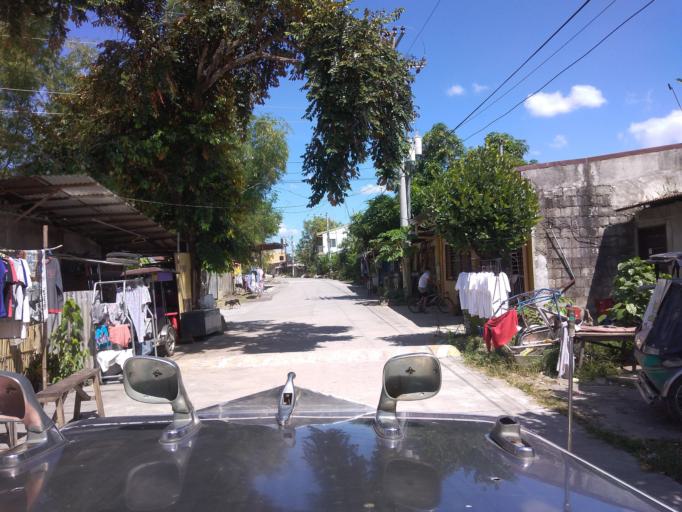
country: PH
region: Central Luzon
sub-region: Province of Pampanga
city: Calibutbut
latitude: 15.0979
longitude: 120.6081
